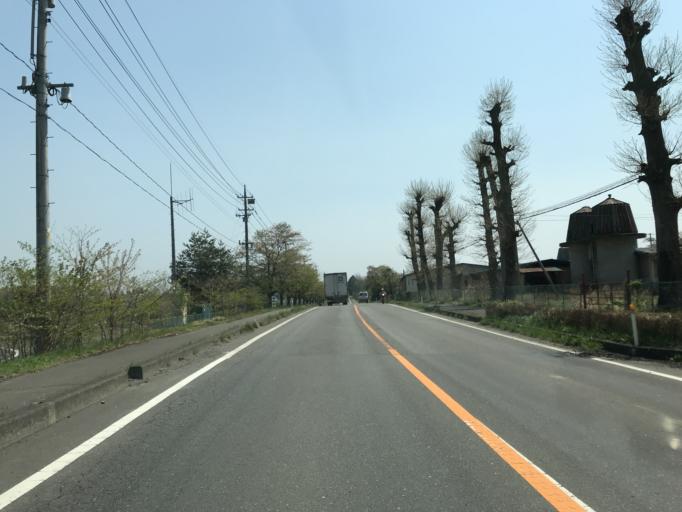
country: JP
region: Fukushima
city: Sukagawa
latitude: 37.1960
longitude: 140.3421
